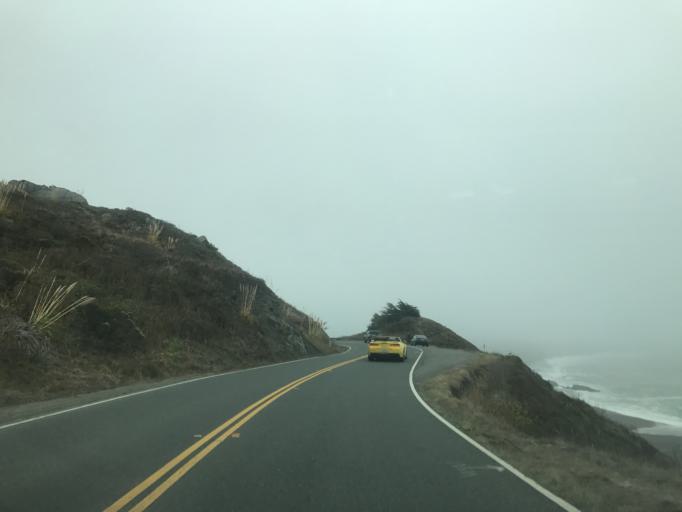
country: US
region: California
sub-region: Sonoma County
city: Monte Rio
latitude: 38.4541
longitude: -123.1322
